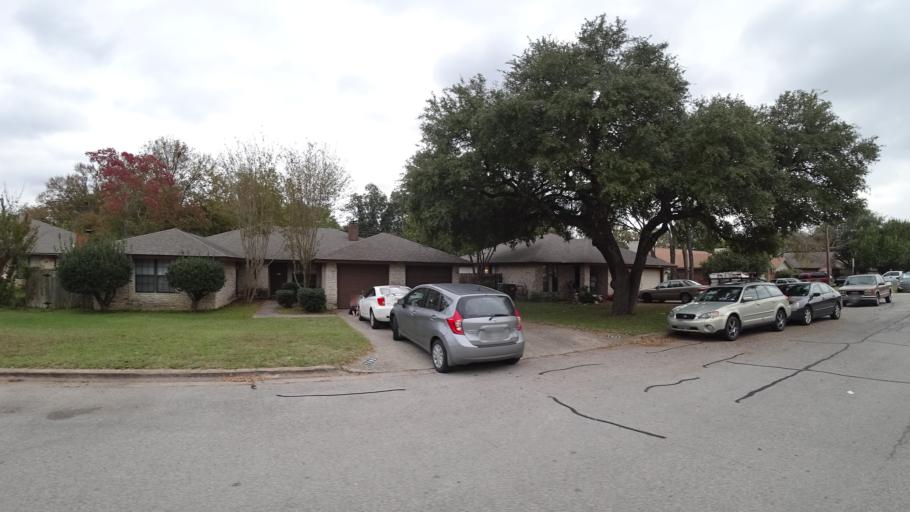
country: US
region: Texas
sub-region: Williamson County
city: Round Rock
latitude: 30.5077
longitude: -97.6929
